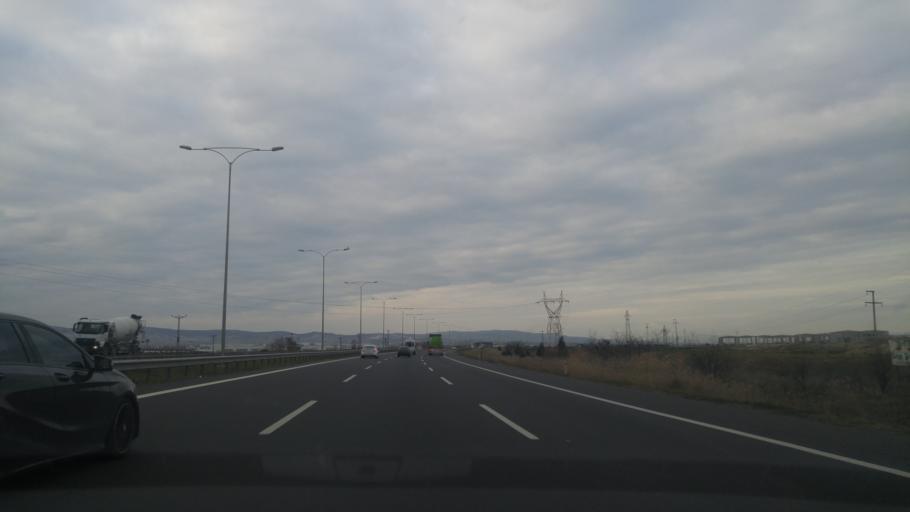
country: TR
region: Ankara
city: Etimesgut
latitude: 40.0517
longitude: 32.5887
